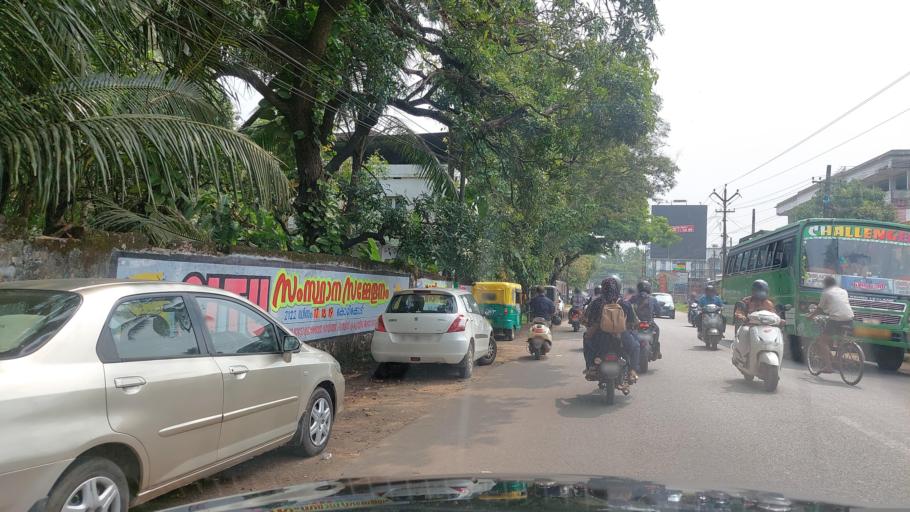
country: IN
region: Kerala
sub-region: Kozhikode
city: Kozhikode
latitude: 11.2916
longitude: 75.7648
